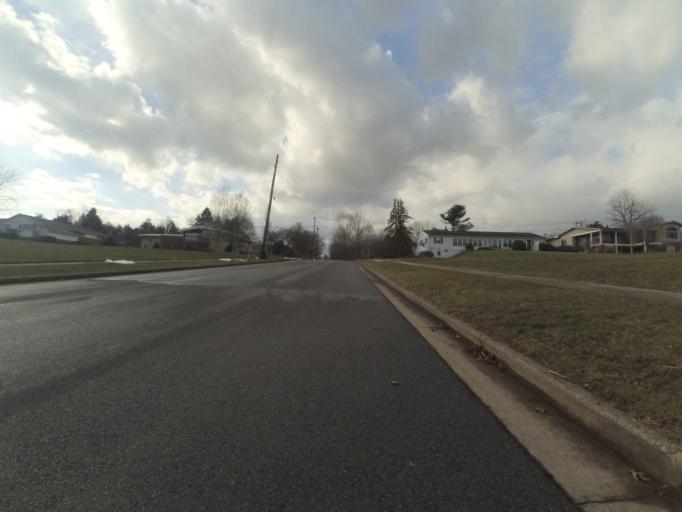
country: US
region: Pennsylvania
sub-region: Centre County
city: State College
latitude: 40.7917
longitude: -77.8366
